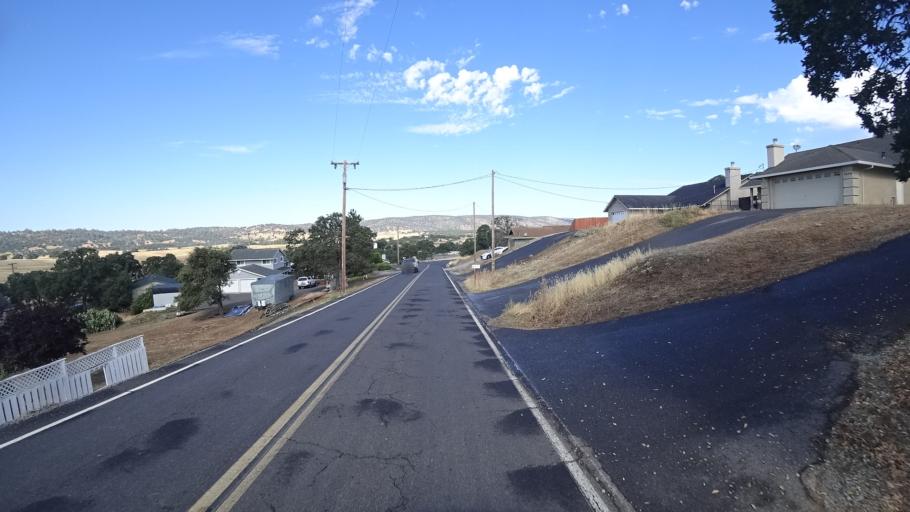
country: US
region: California
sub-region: Calaveras County
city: Copperopolis
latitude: 37.9085
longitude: -120.6125
